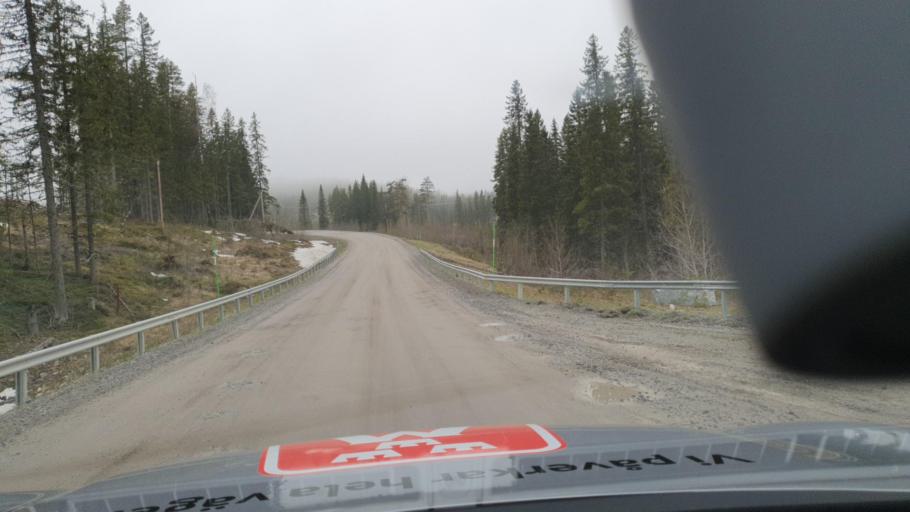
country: SE
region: Vaesternorrland
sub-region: OErnskoeldsviks Kommun
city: Husum
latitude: 63.6237
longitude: 19.0439
